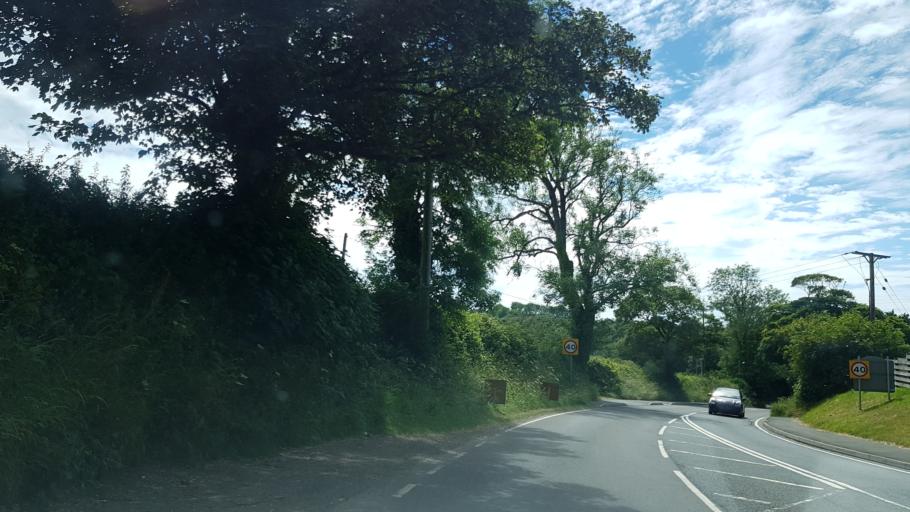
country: GB
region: Wales
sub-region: Pembrokeshire
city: Haverfordwest
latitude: 51.8210
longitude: -4.9515
